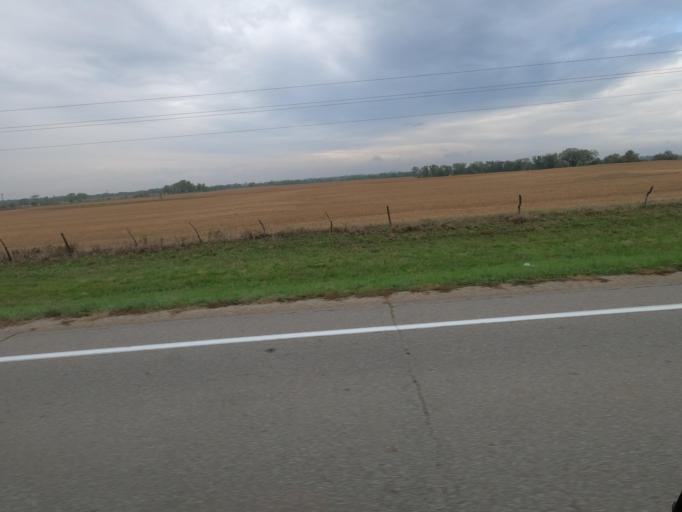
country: US
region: Iowa
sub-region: Henry County
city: Mount Pleasant
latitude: 40.8136
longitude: -91.7163
